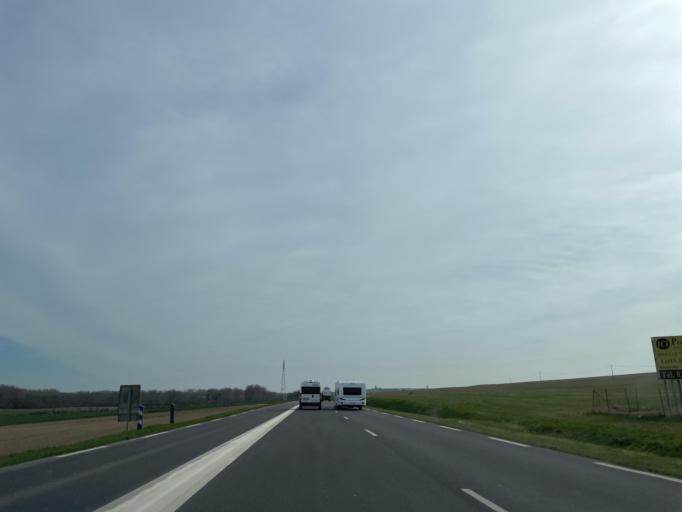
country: FR
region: Champagne-Ardenne
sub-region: Departement de l'Aube
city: Villenauxe-la-Grande
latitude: 48.5106
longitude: 3.6086
